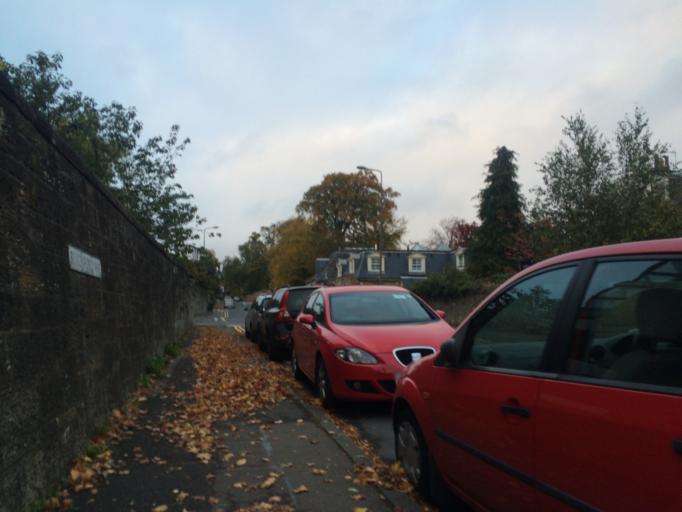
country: GB
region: Scotland
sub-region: Edinburgh
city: Edinburgh
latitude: 55.9296
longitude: -3.1891
